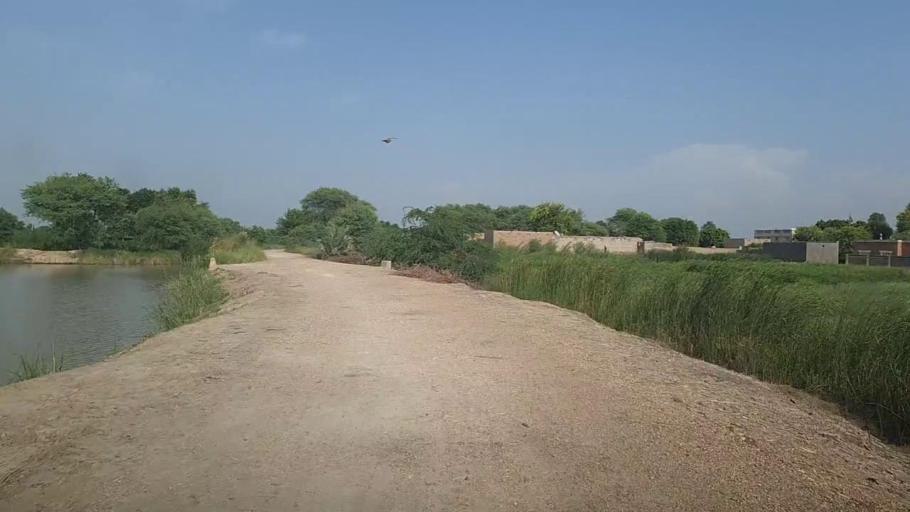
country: PK
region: Sindh
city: Ubauro
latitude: 28.1664
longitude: 69.7760
